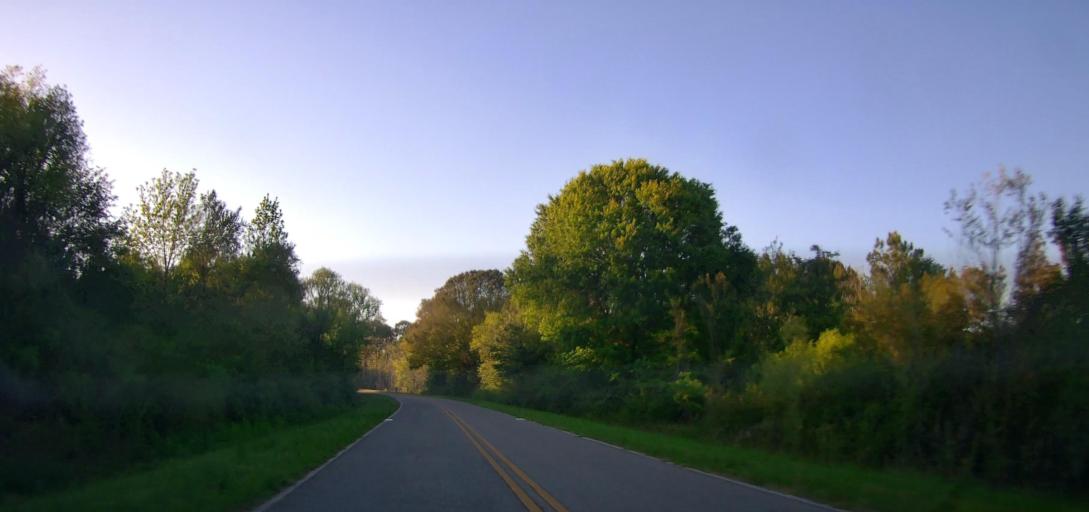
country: US
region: Georgia
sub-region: Ben Hill County
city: Fitzgerald
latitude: 31.6885
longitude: -83.2312
